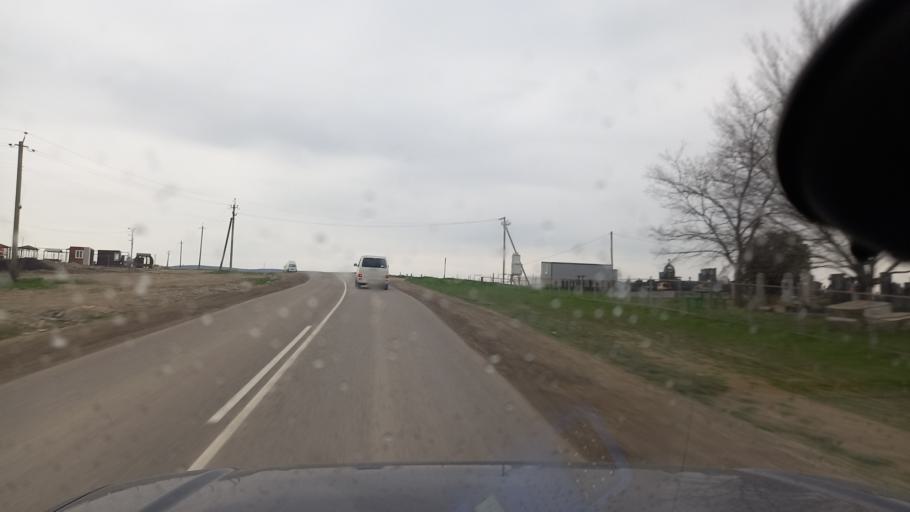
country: RU
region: Krasnodarskiy
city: Anapskaya
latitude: 44.8851
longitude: 37.4533
